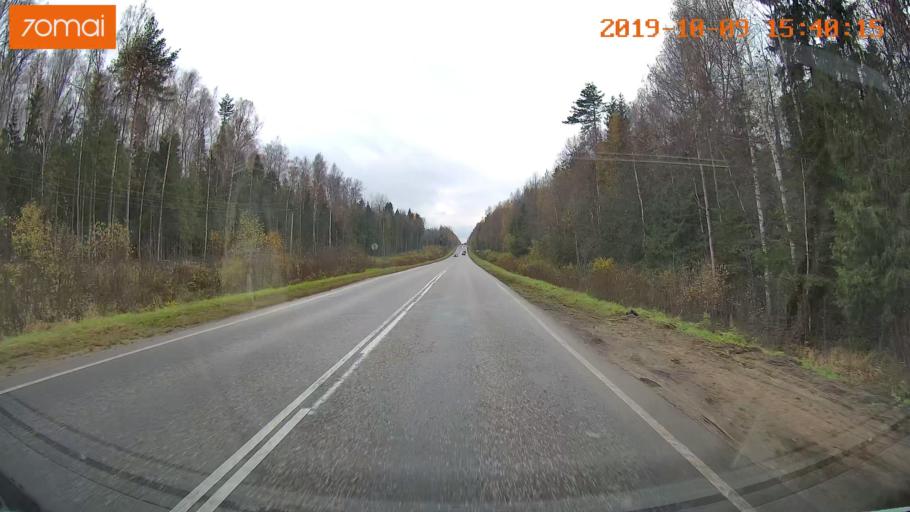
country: RU
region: Kostroma
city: Oktyabr'skiy
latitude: 57.8894
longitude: 41.1481
